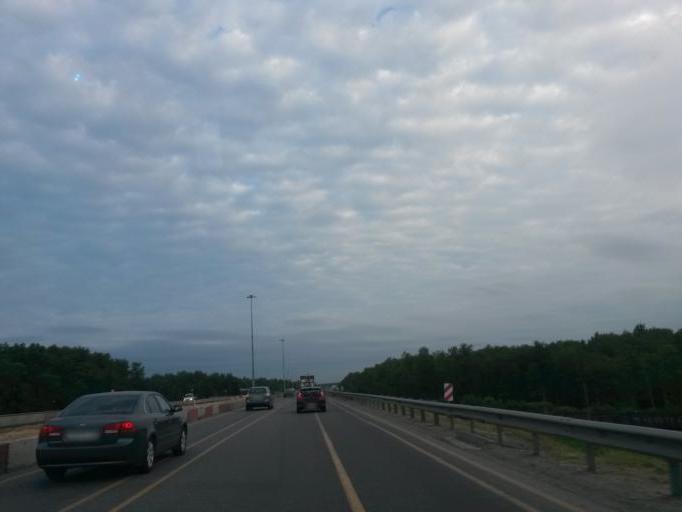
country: RU
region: Moskovskaya
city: Lyubuchany
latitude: 55.2078
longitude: 37.5351
